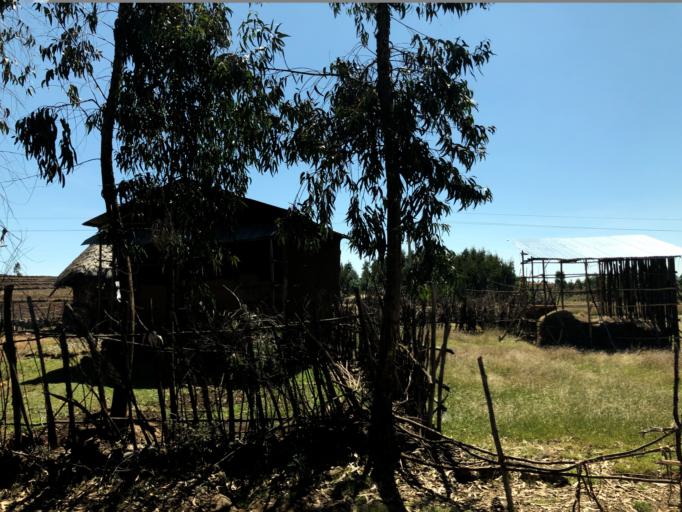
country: ET
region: Amhara
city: Lalibela
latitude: 11.6786
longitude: 38.9005
